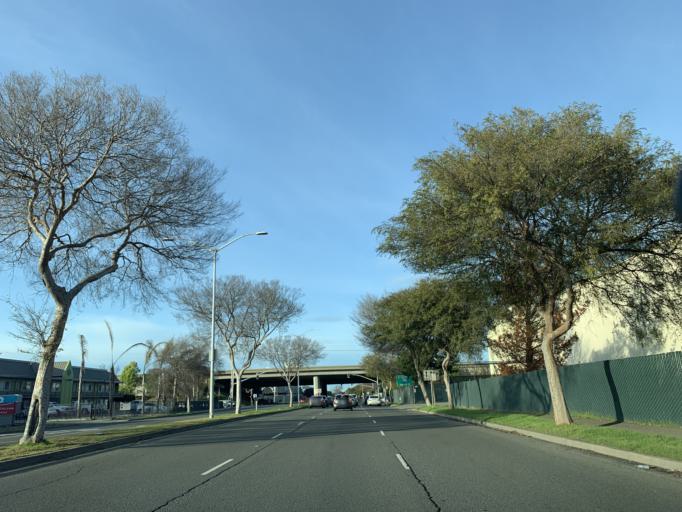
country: US
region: California
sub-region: Contra Costa County
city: Richmond
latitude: 37.9257
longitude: -122.3781
